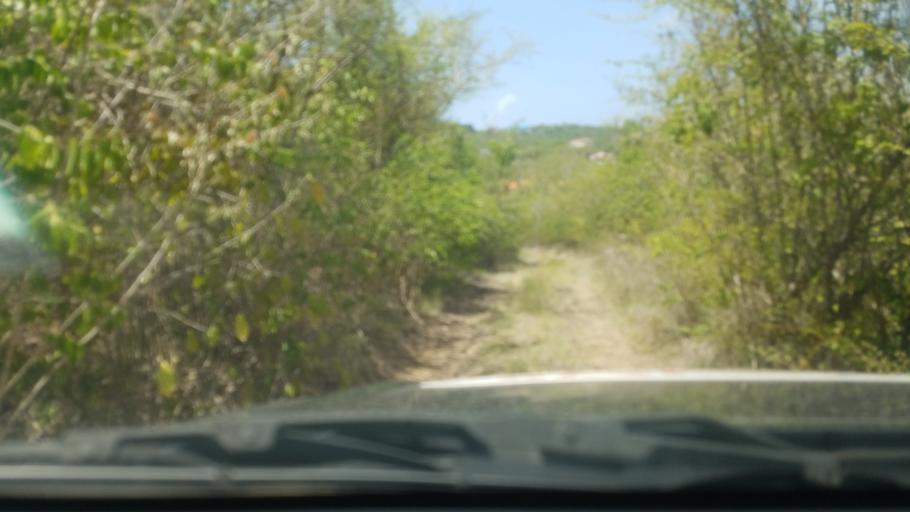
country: LC
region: Vieux-Fort
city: Vieux Fort
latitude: 13.7225
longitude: -60.9495
